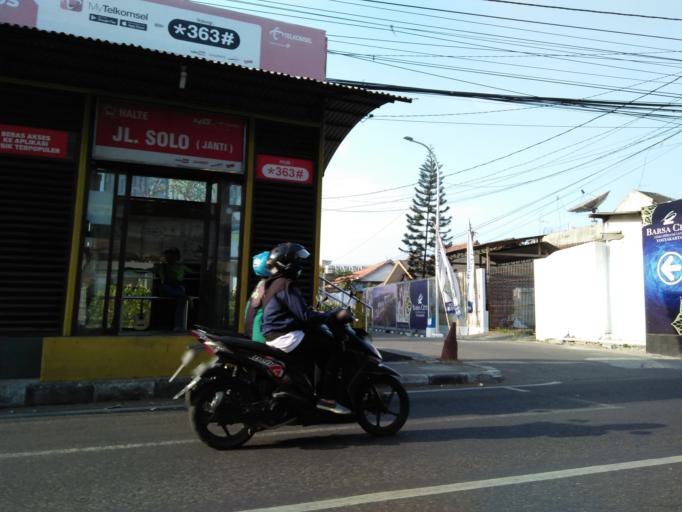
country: ID
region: Daerah Istimewa Yogyakarta
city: Depok
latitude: -7.7832
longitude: 110.4117
